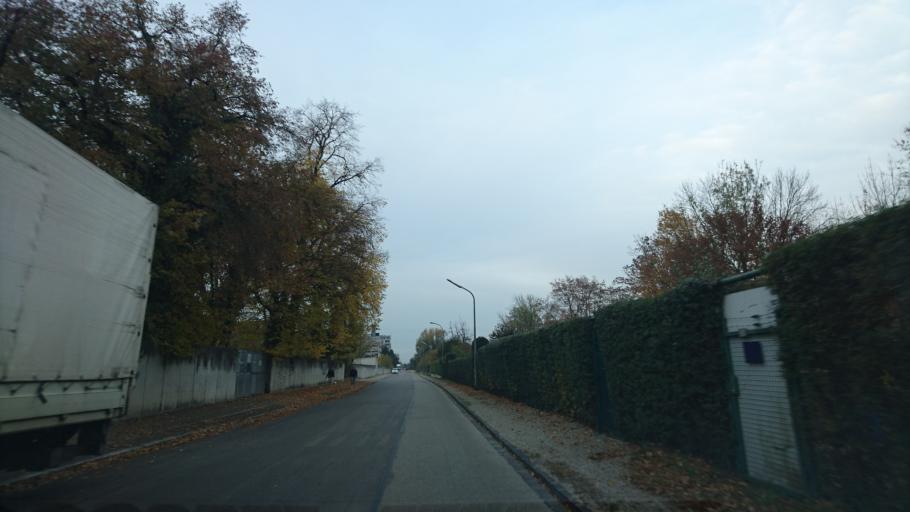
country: DE
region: Bavaria
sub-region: Swabia
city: Augsburg
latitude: 48.3869
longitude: 10.8858
